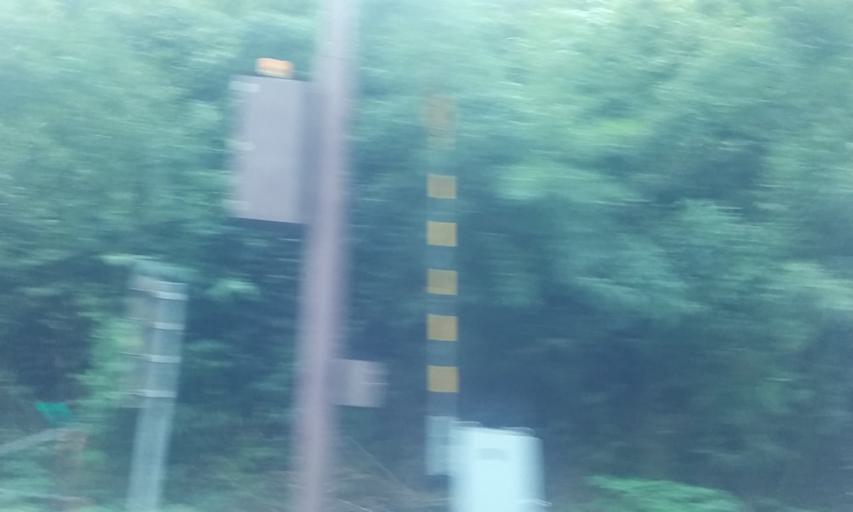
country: JP
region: Kyoto
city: Maizuru
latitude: 35.4502
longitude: 135.2826
